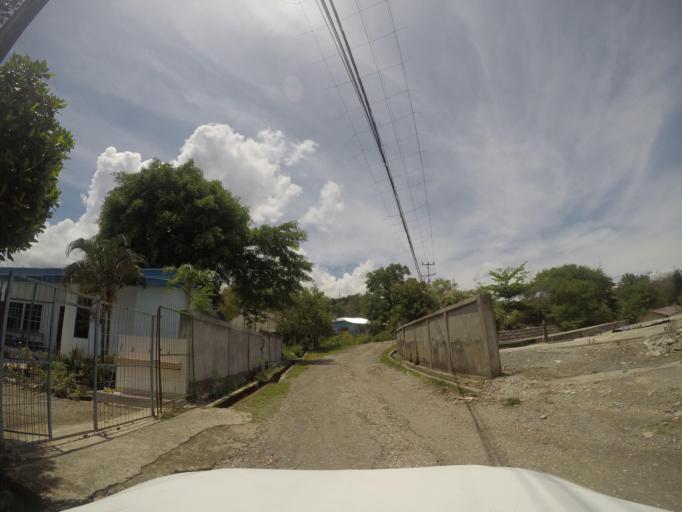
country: TL
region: Bobonaro
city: Maliana
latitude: -8.9956
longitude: 125.2250
